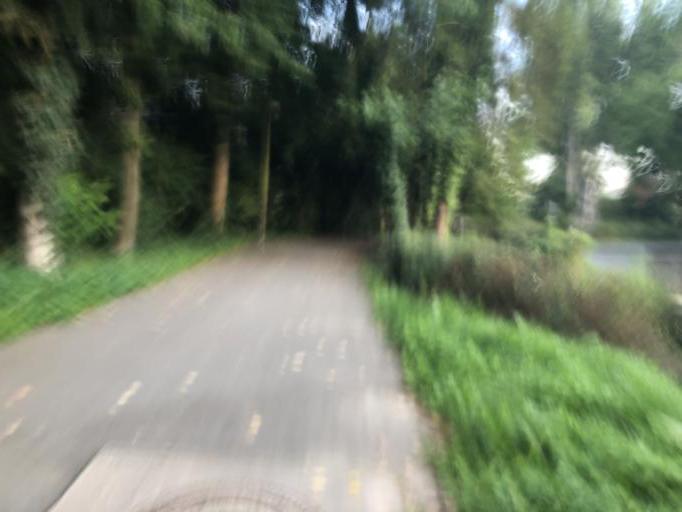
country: DE
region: Bavaria
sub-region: Regierungsbezirk Mittelfranken
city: Erlangen
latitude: 49.5875
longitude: 10.9601
